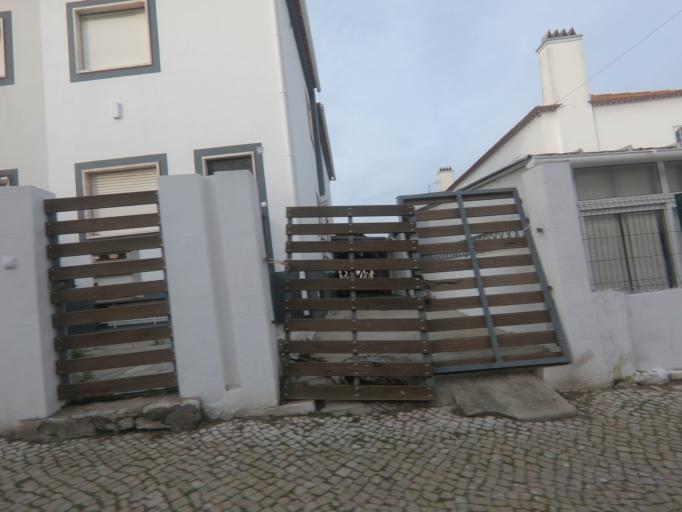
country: PT
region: Setubal
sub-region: Setubal
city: Setubal
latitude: 38.5246
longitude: -8.8777
